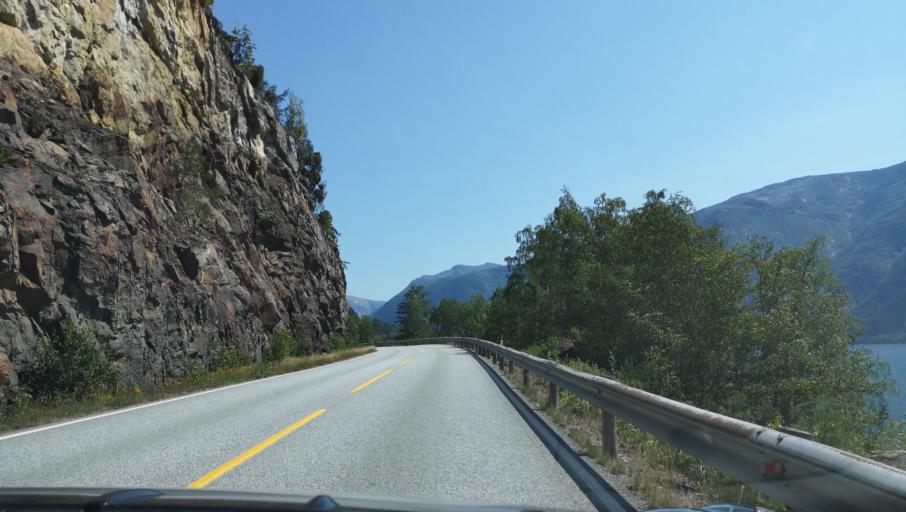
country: NO
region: Hordaland
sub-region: Ulvik
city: Ulvik
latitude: 60.4892
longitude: 6.8454
